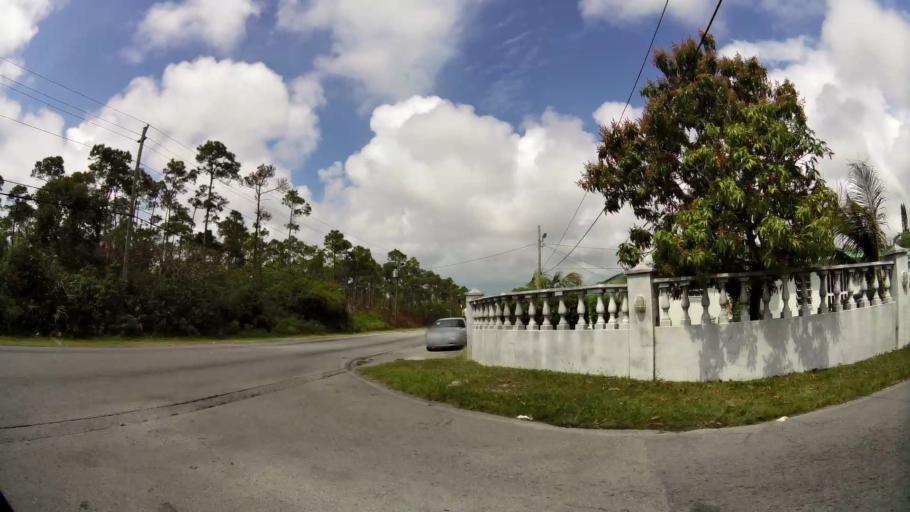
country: BS
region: Freeport
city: Freeport
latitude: 26.5128
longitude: -78.6927
